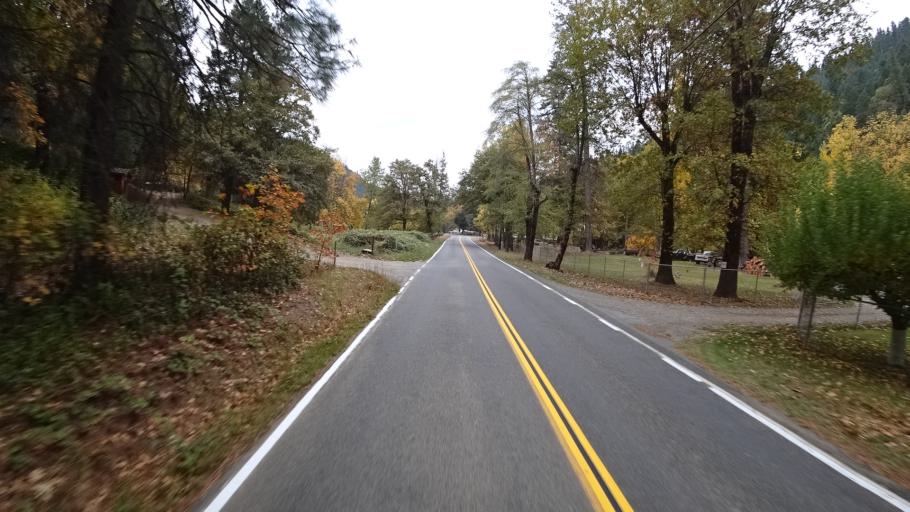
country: US
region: California
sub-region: Siskiyou County
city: Happy Camp
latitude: 41.8305
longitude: -123.3837
